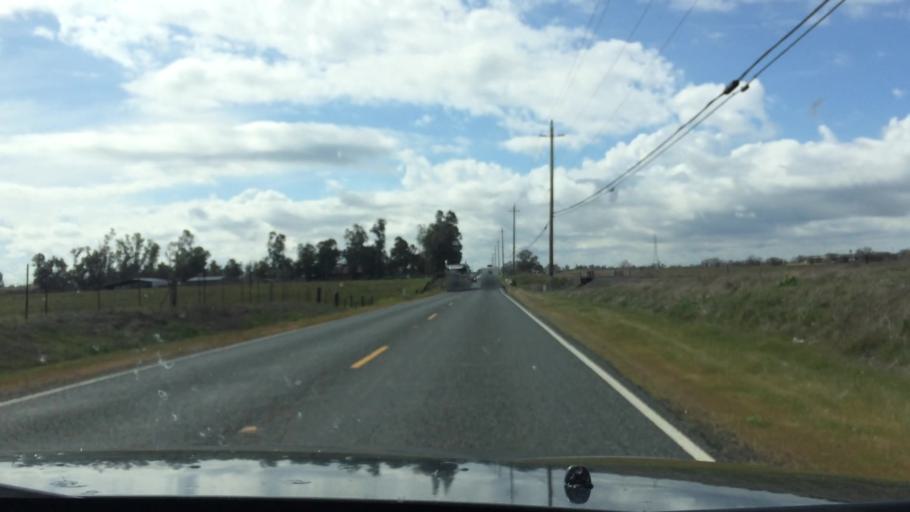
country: US
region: California
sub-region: Sacramento County
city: Herald
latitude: 38.3104
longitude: -121.2181
